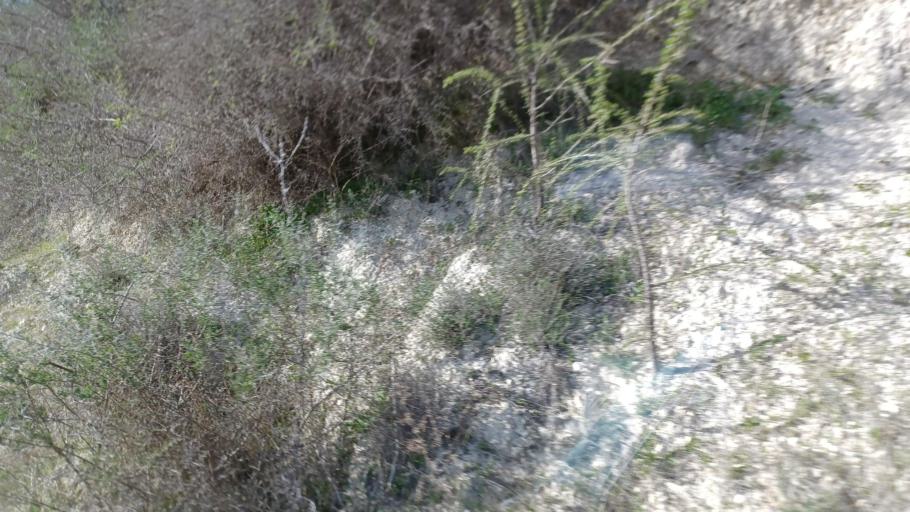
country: CY
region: Limassol
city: Pachna
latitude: 34.8423
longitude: 32.7192
